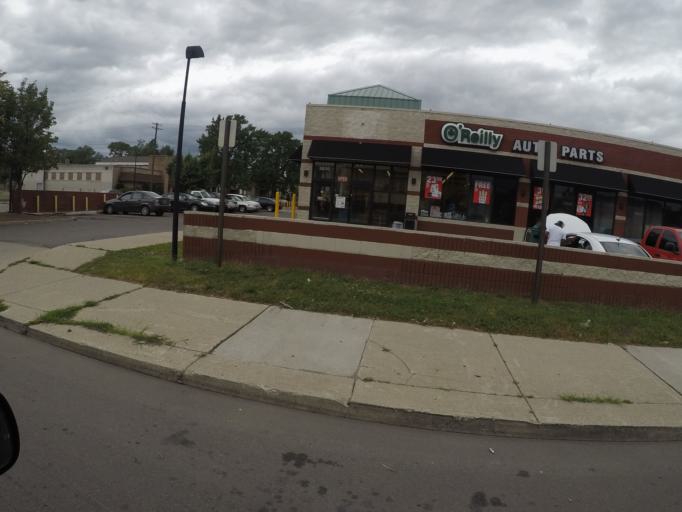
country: US
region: Michigan
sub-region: Wayne County
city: Detroit
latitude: 42.3225
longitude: -83.0903
